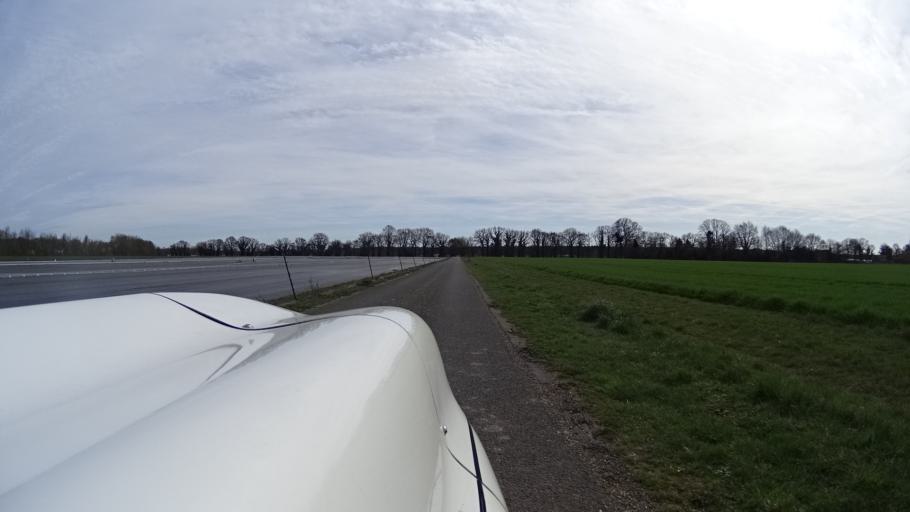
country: DE
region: North Rhine-Westphalia
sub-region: Regierungsbezirk Dusseldorf
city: Kevelaer
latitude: 51.5470
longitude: 6.2132
